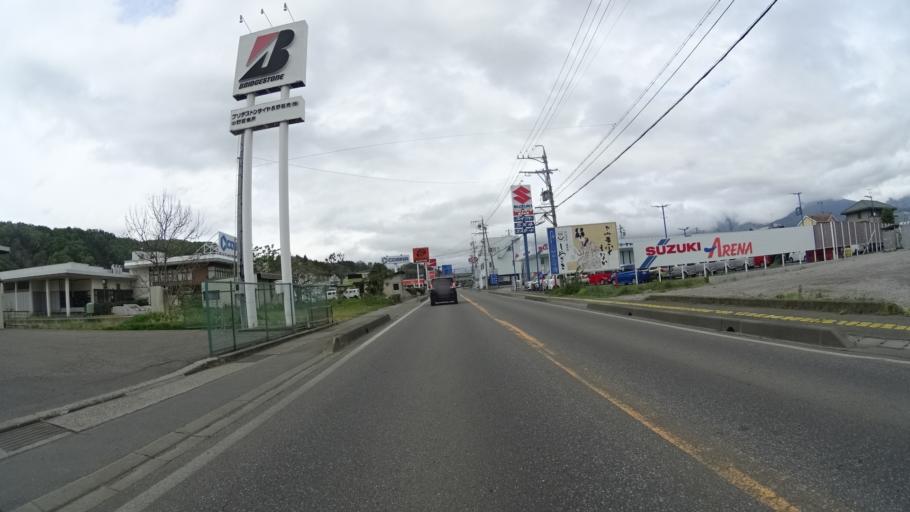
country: JP
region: Nagano
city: Nakano
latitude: 36.7505
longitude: 138.3505
